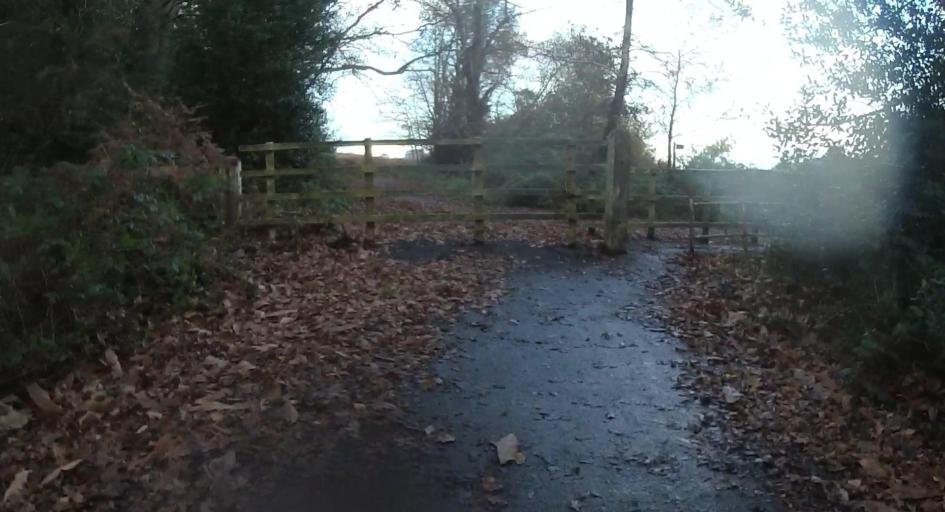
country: GB
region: England
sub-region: Bracknell Forest
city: Crowthorne
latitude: 51.3617
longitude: -0.7797
